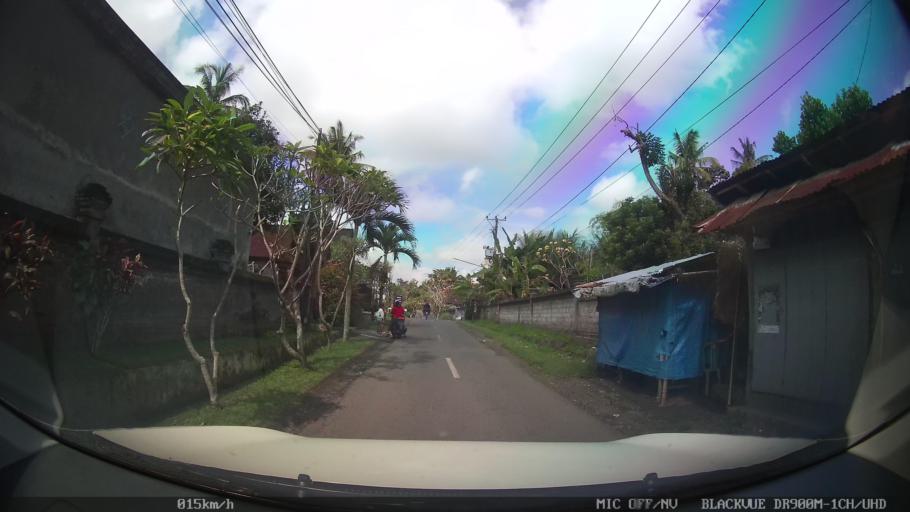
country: ID
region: Bali
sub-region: Kabupaten Gianyar
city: Ubud
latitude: -8.5216
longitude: 115.2993
